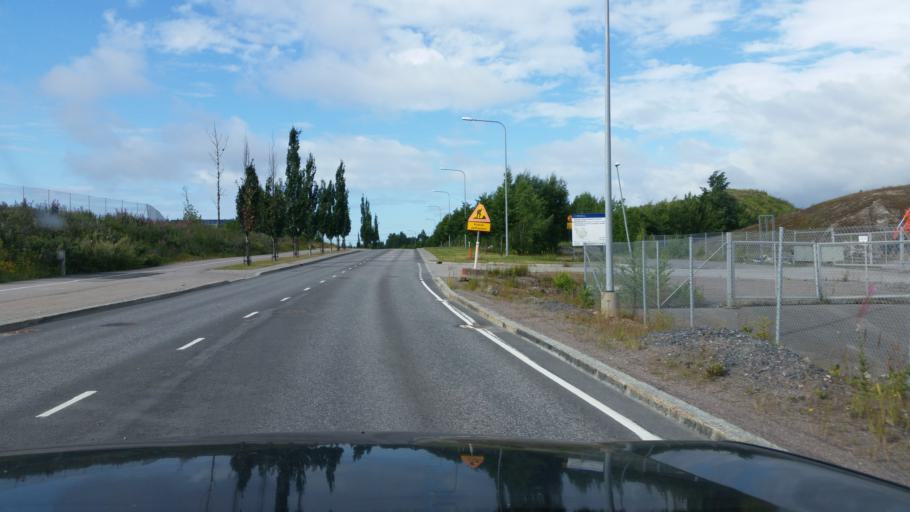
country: FI
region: Uusimaa
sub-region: Helsinki
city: Vantaa
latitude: 60.2243
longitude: 25.1648
